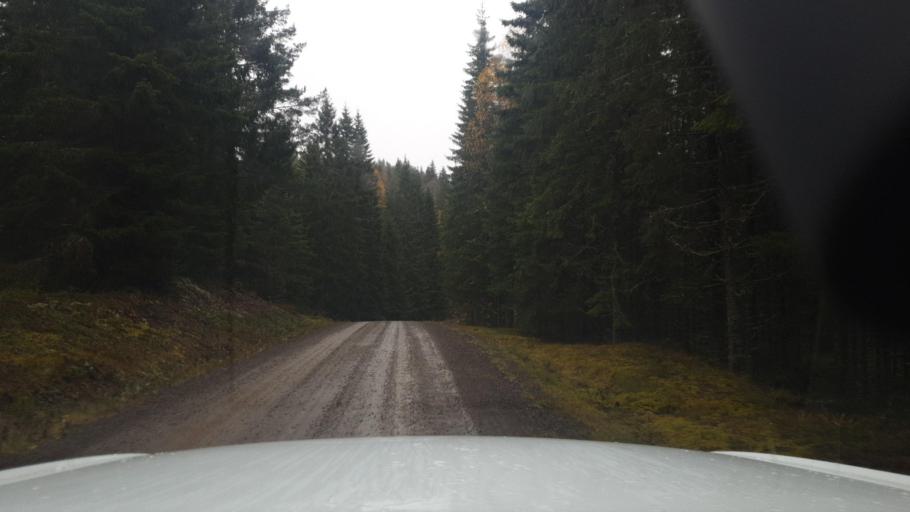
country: SE
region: Vaermland
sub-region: Sunne Kommun
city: Sunne
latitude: 59.8615
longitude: 12.8706
